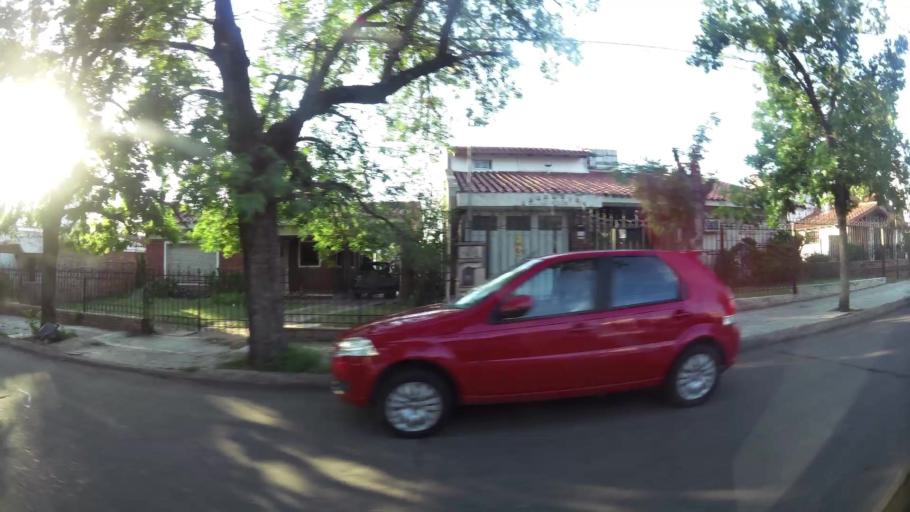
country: AR
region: Cordoba
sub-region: Departamento de Capital
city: Cordoba
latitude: -31.3772
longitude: -64.2327
